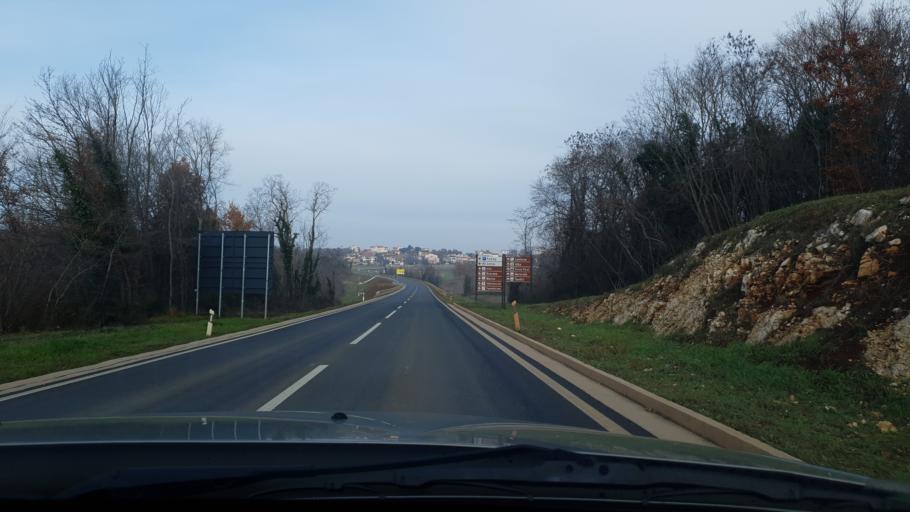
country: HR
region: Istarska
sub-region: Grad Porec
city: Porec
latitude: 45.2189
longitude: 13.6232
